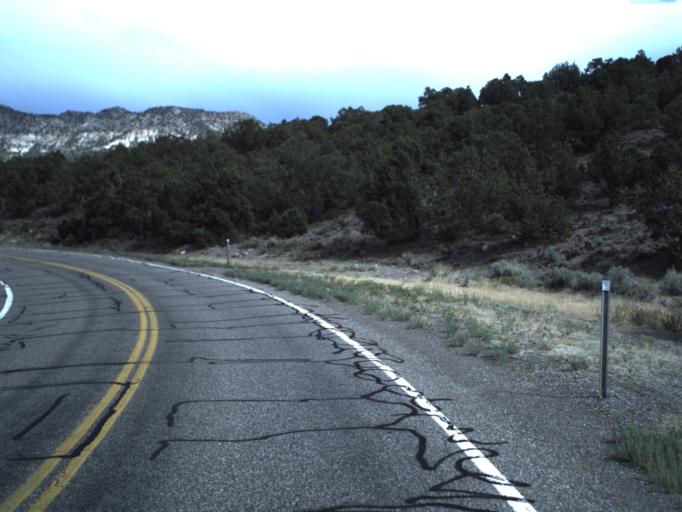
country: US
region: Utah
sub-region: Sevier County
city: Aurora
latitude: 38.7772
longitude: -111.9371
